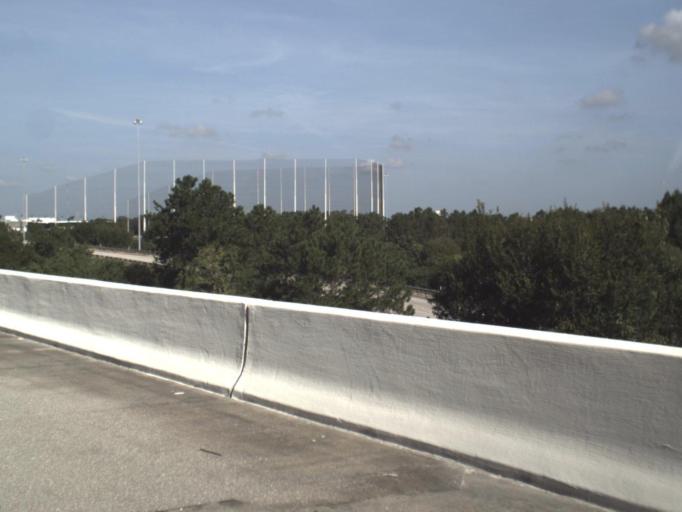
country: US
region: Florida
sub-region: Hillsborough County
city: Brandon
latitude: 27.9272
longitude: -82.3285
